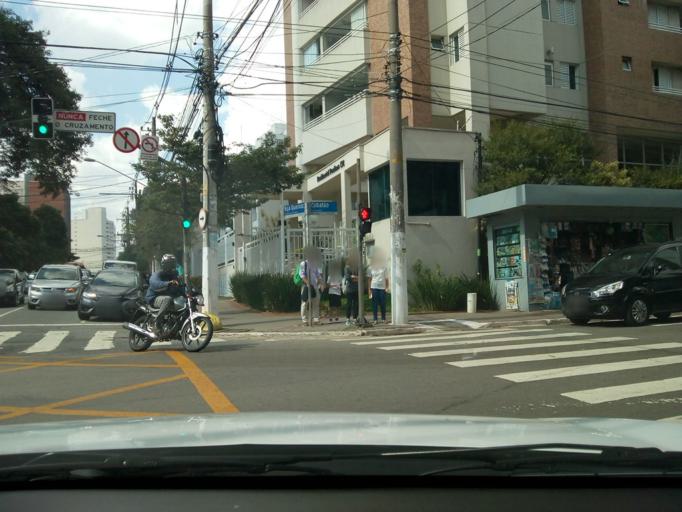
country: BR
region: Sao Paulo
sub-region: Sao Paulo
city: Sao Paulo
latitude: -23.5787
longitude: -46.6424
